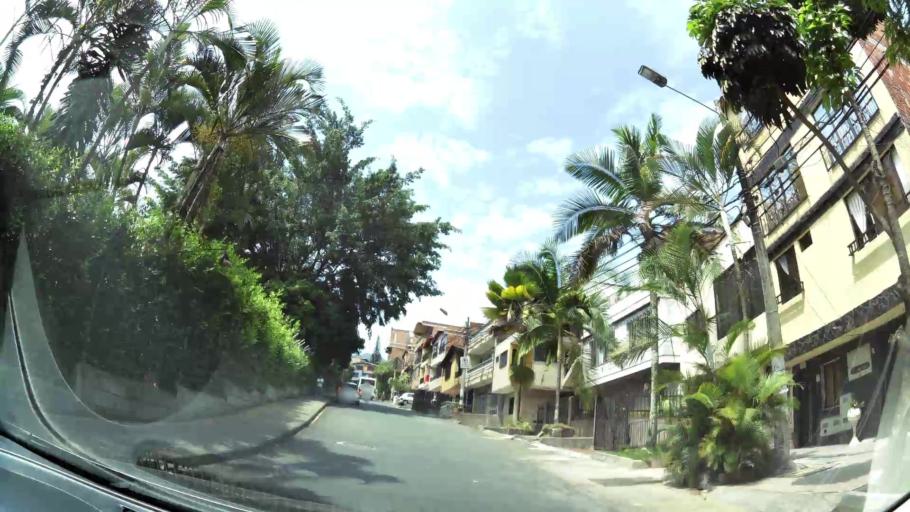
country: CO
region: Antioquia
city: Bello
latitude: 6.3189
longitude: -75.5640
